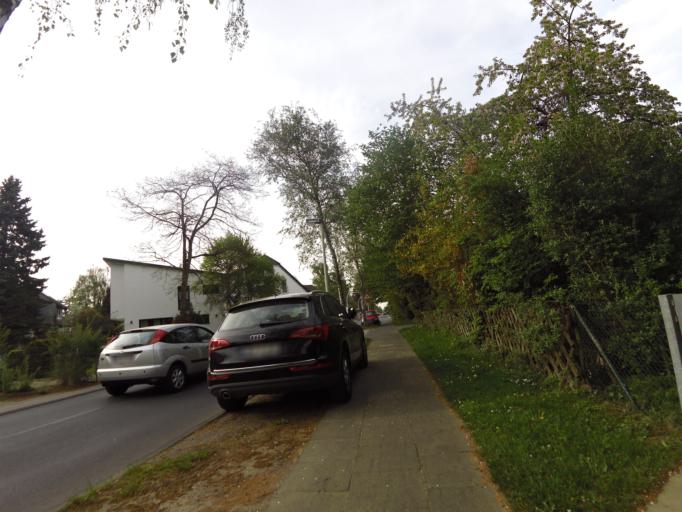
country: DE
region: North Rhine-Westphalia
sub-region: Regierungsbezirk Koln
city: Bonn
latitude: 50.6903
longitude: 7.0853
